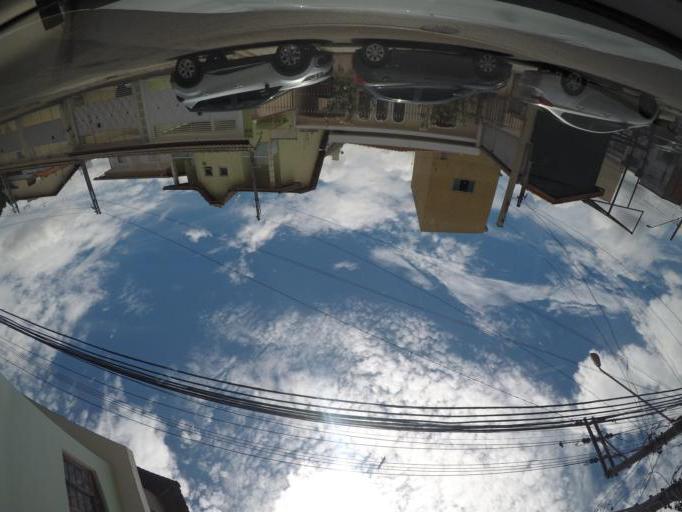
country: BR
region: Sao Paulo
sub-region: Guarulhos
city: Guarulhos
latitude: -23.4631
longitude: -46.5243
